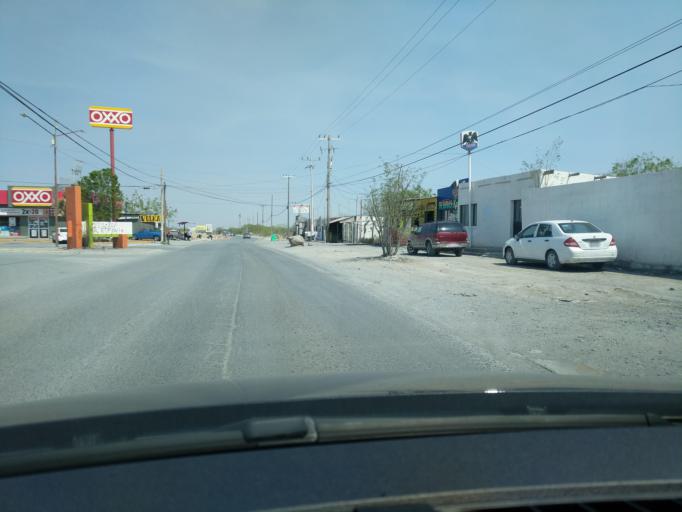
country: MX
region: Nuevo Leon
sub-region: Garcia
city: Valle de Lincoln
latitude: 25.7930
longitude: -100.4748
